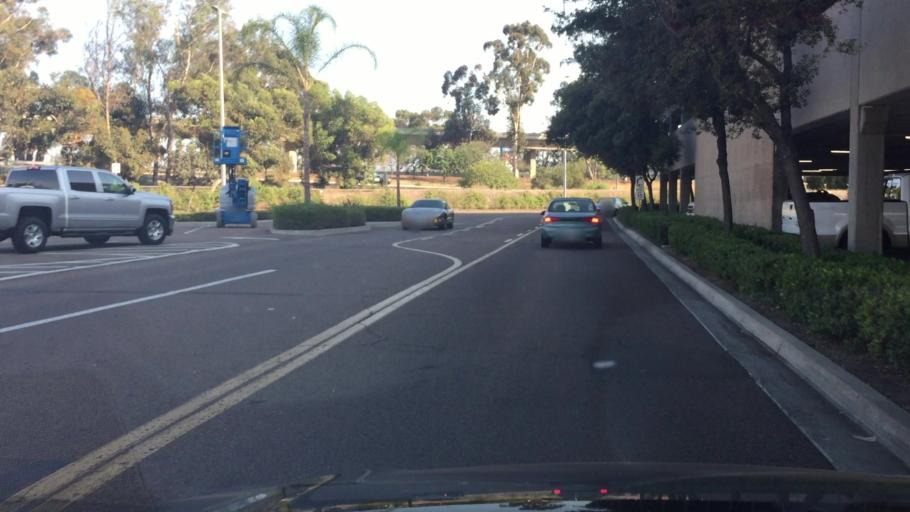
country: US
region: California
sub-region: San Diego County
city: El Cajon
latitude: 32.8049
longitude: -116.9641
